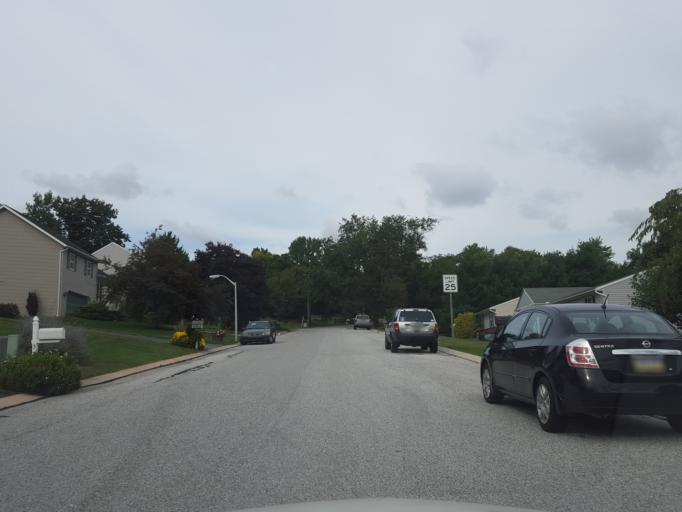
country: US
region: Pennsylvania
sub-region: York County
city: Red Lion
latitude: 39.8920
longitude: -76.6154
